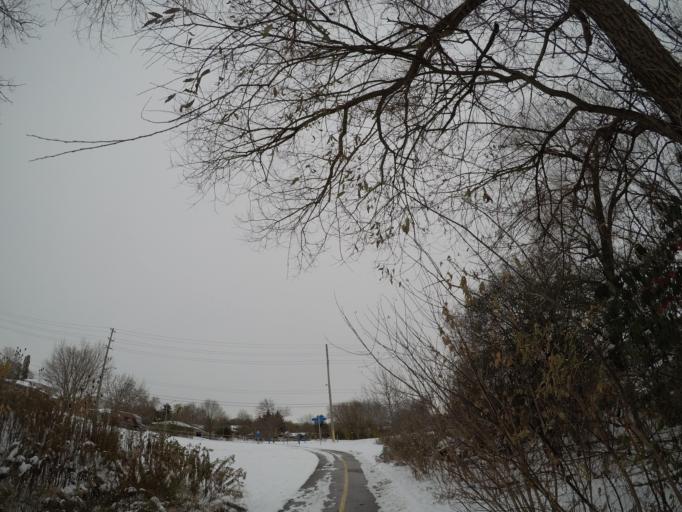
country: CA
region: Ontario
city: Waterloo
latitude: 43.4806
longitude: -80.5149
